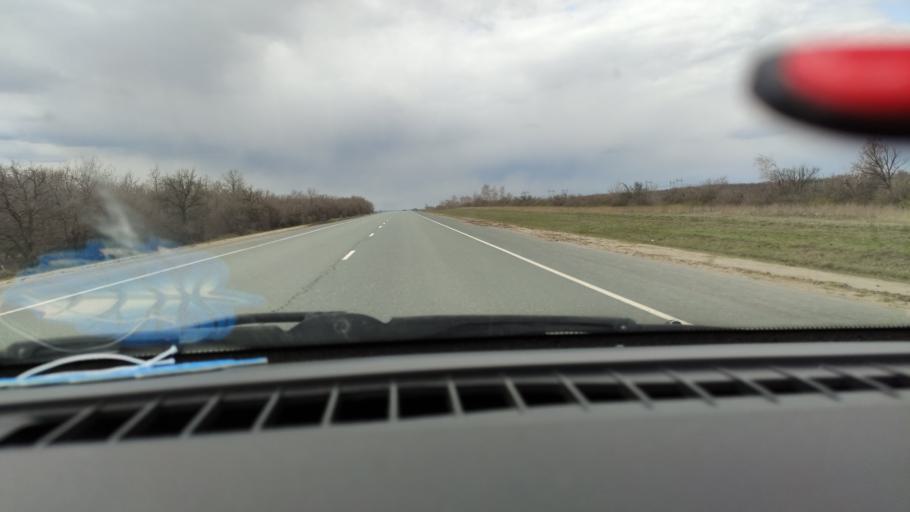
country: RU
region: Saratov
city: Yelshanka
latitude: 51.8214
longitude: 46.3350
